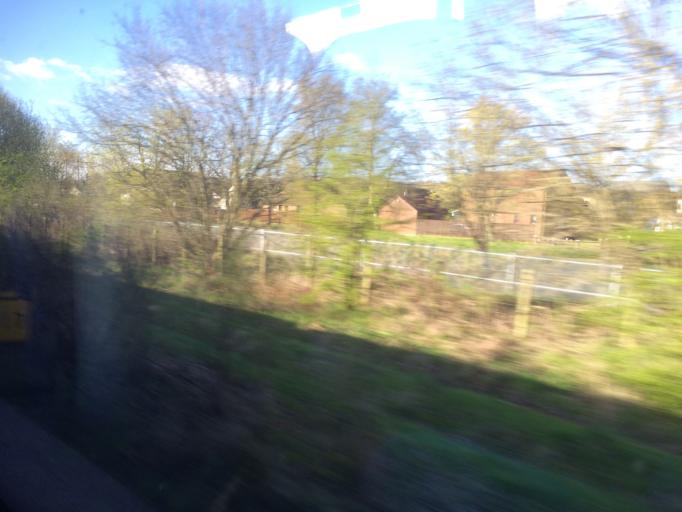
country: GB
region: Scotland
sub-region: Stirling
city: Bannockburn
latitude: 56.1038
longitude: -3.9172
